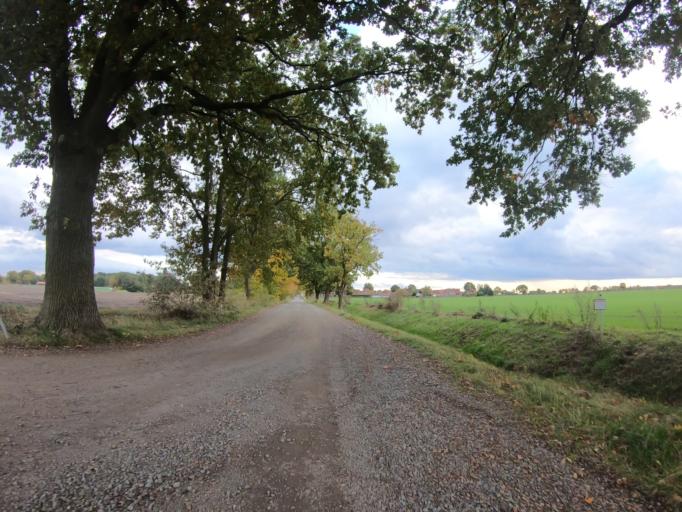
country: DE
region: Lower Saxony
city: Wagenhoff
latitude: 52.5223
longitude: 10.5251
